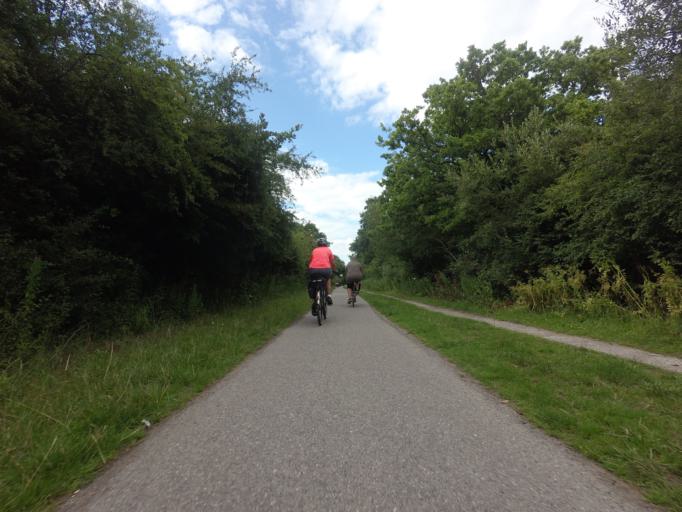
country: GB
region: England
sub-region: East Sussex
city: Hailsham
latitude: 50.8414
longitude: 0.2529
